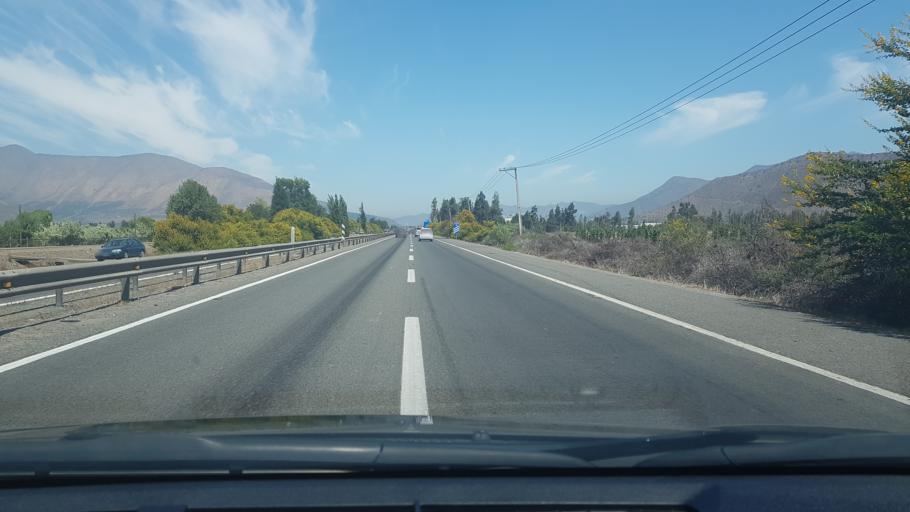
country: CL
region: Valparaiso
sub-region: Provincia de San Felipe
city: Llaillay
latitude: -32.8529
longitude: -70.9301
